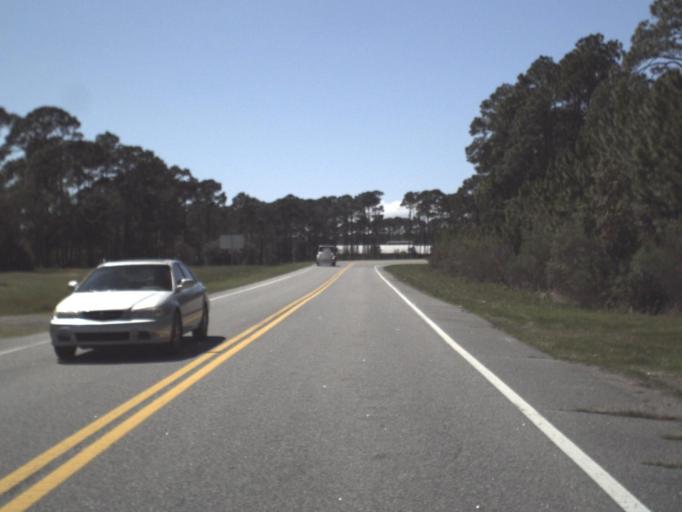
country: US
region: Florida
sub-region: Franklin County
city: Carrabelle
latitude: 29.9172
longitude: -84.5125
